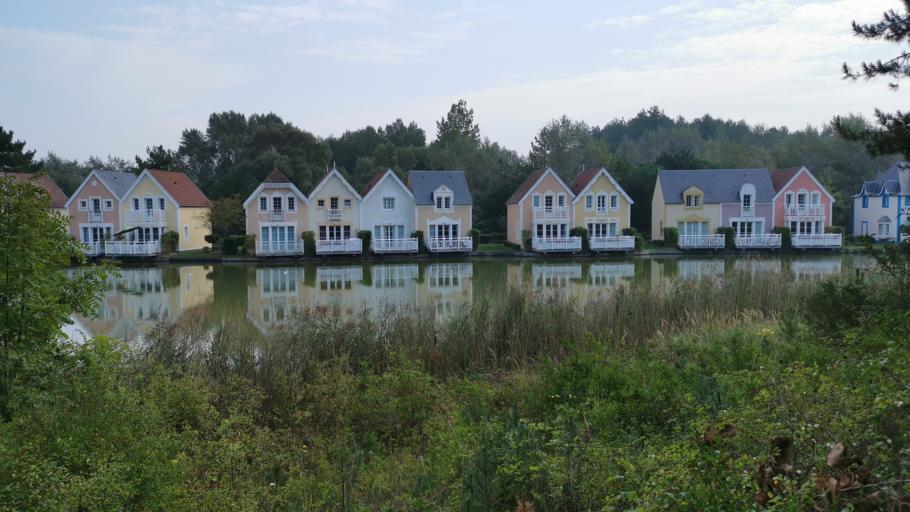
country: FR
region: Picardie
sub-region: Departement de la Somme
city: Fort-Mahon-Plage
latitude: 50.3289
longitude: 1.5648
